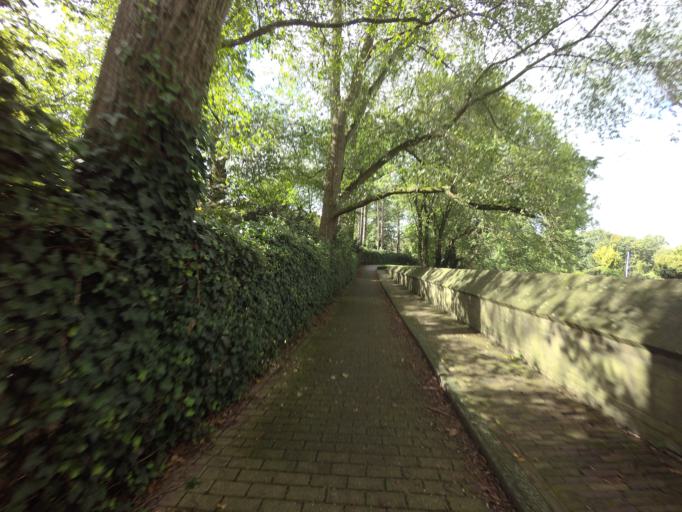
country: NL
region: North Holland
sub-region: Gemeente Enkhuizen
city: Enkhuizen
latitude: 52.7097
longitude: 5.2895
